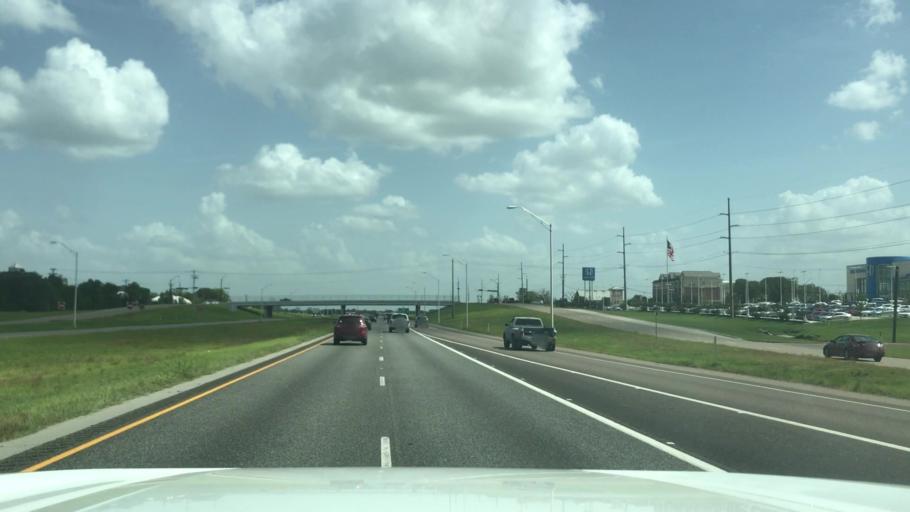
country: US
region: Texas
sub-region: Brazos County
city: College Station
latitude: 30.6215
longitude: -96.2973
